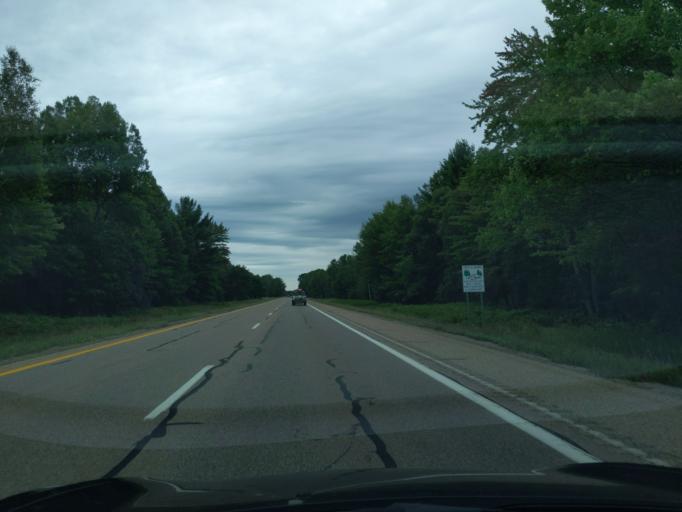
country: US
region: Michigan
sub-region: Roscommon County
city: Houghton Lake
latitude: 44.2526
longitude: -84.8041
